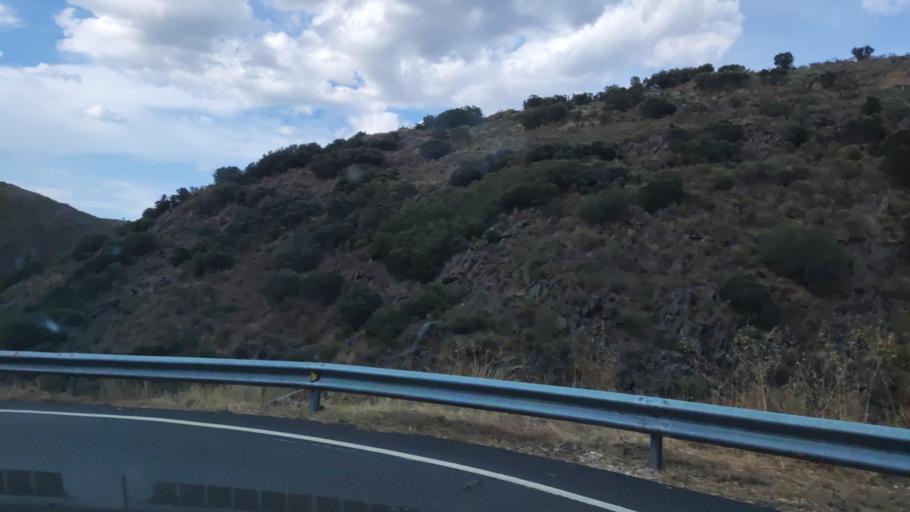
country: ES
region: Castille and Leon
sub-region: Provincia de Salamanca
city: Pastores
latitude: 40.4956
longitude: -6.4915
